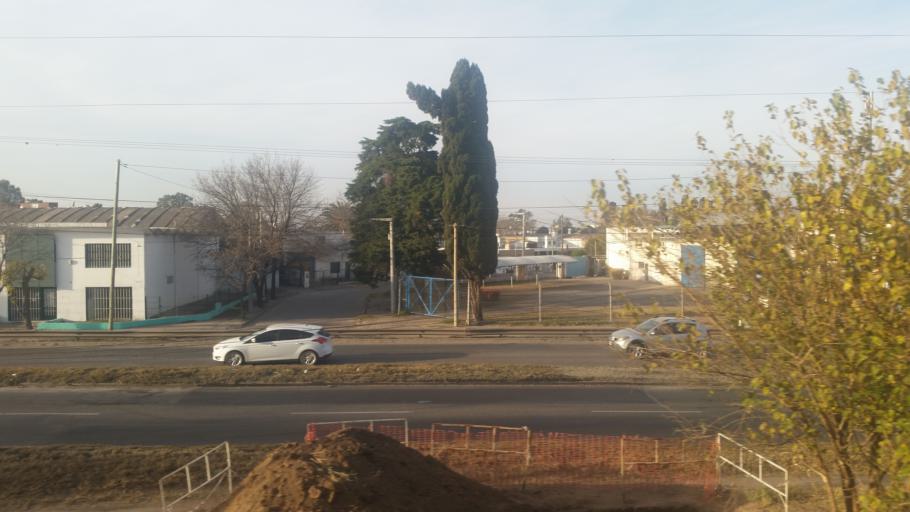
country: AR
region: Cordoba
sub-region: Departamento de Capital
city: Cordoba
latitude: -31.4480
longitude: -64.1206
